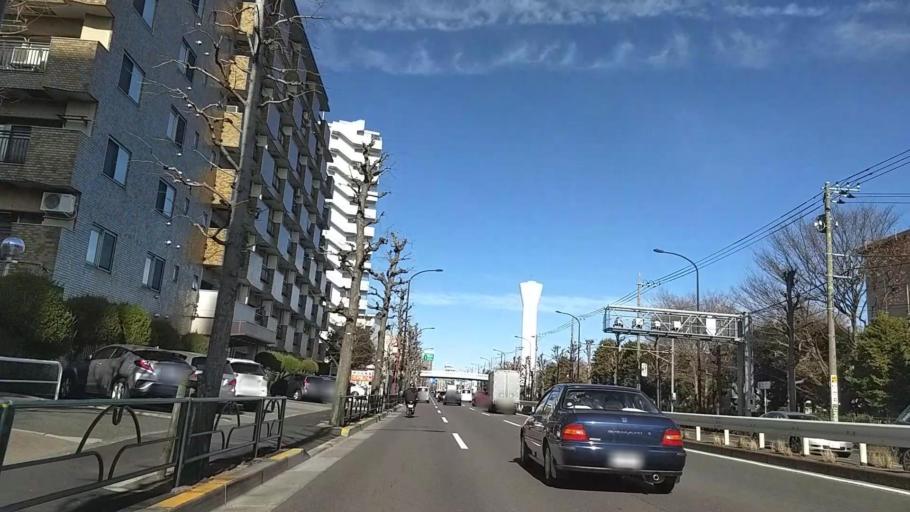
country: JP
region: Tokyo
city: Mitaka-shi
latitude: 35.6642
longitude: 139.6138
